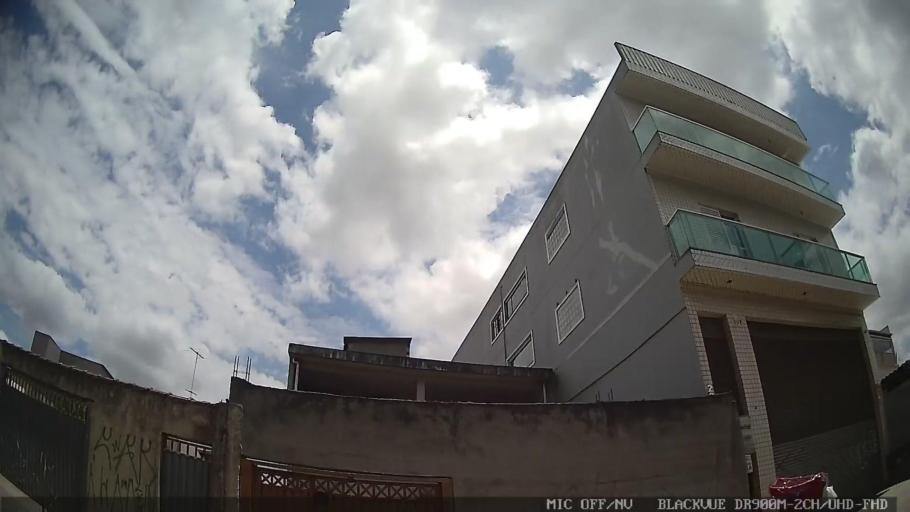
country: BR
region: Sao Paulo
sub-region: Guarulhos
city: Guarulhos
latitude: -23.5303
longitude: -46.4886
